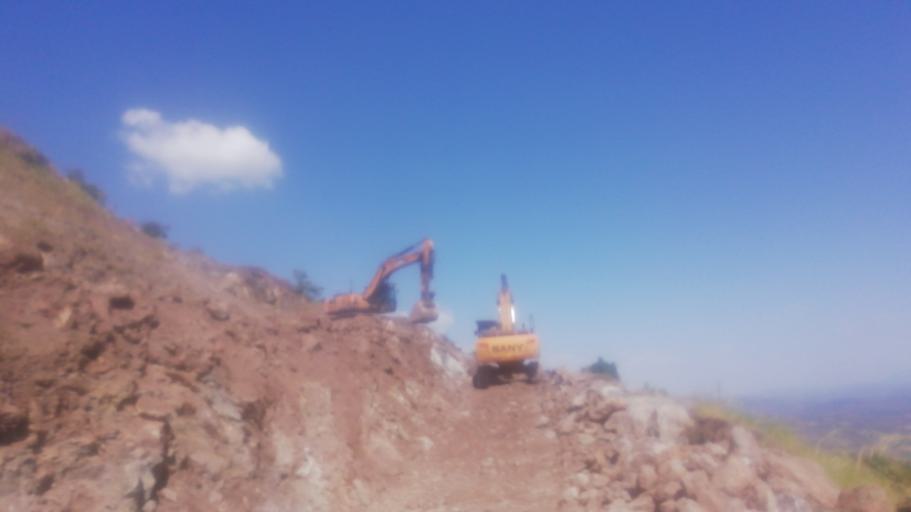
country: ET
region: Amhara
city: Addiet Canna
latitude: 11.2298
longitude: 37.8887
